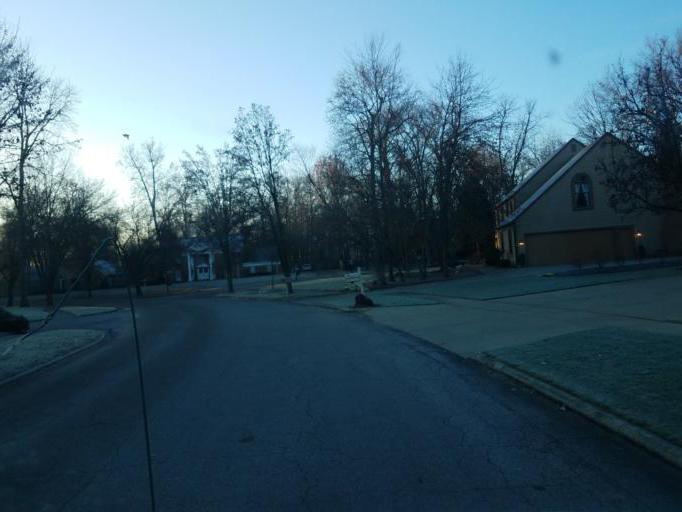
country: US
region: Ohio
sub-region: Marion County
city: Marion
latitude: 40.5623
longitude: -83.0877
